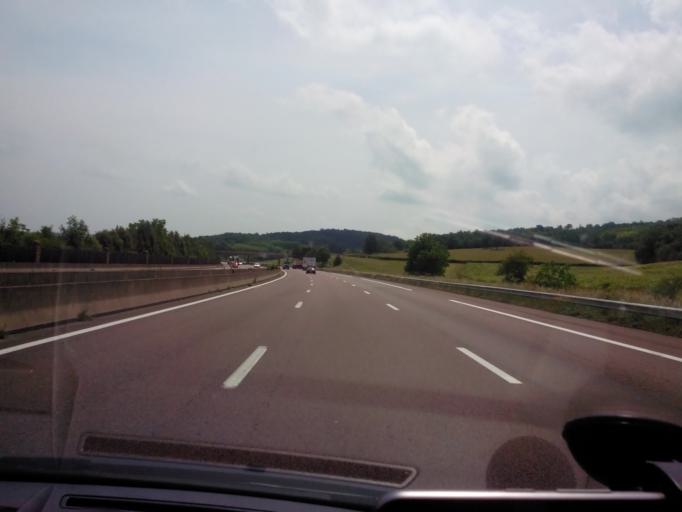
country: FR
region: Bourgogne
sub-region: Departement de Saone-et-Loire
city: Sennecey-le-Grand
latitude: 46.6253
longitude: 4.8599
